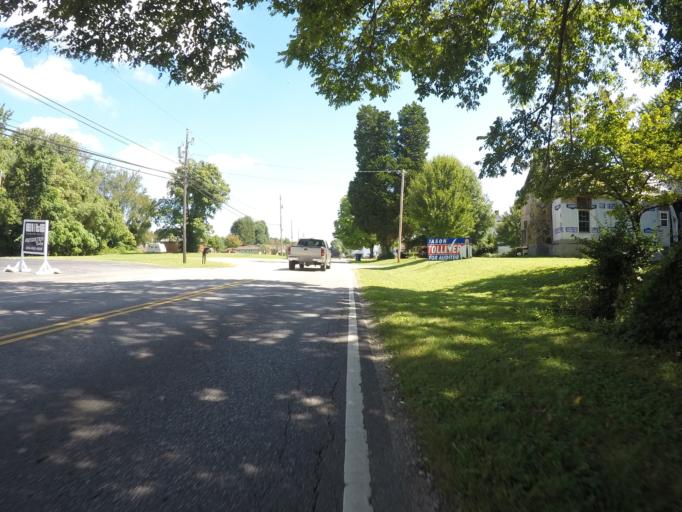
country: US
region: West Virginia
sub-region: Cabell County
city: Huntington
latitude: 38.4229
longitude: -82.4800
